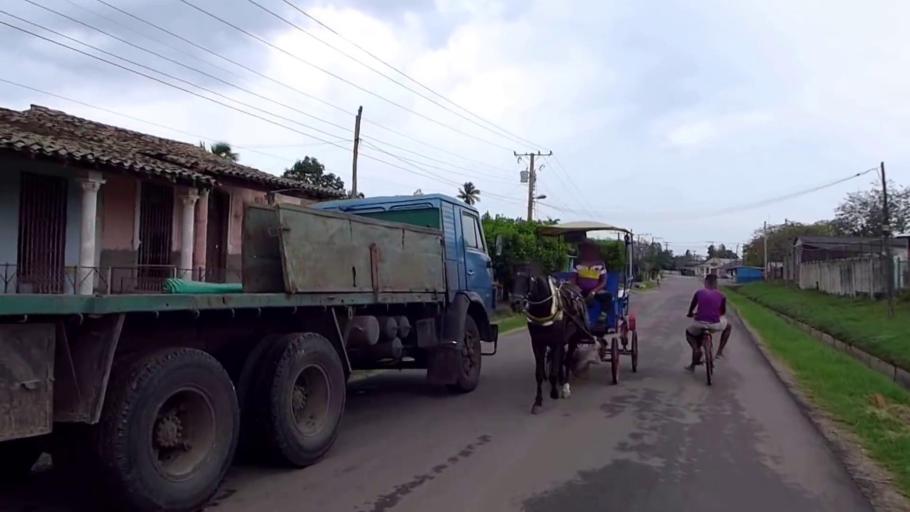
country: CU
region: Camaguey
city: Camaguey
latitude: 21.3876
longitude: -77.9341
